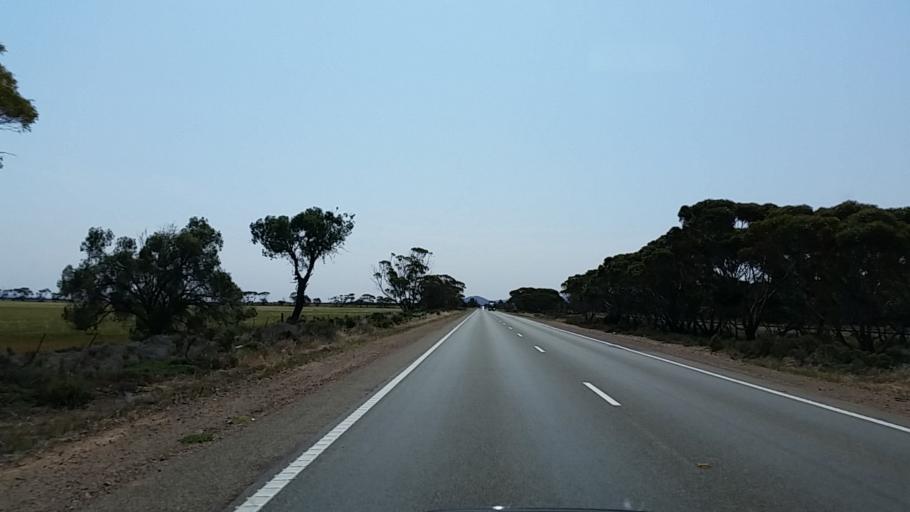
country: AU
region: South Australia
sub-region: Port Pirie City and Dists
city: Port Pirie
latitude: -32.9362
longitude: 137.9824
